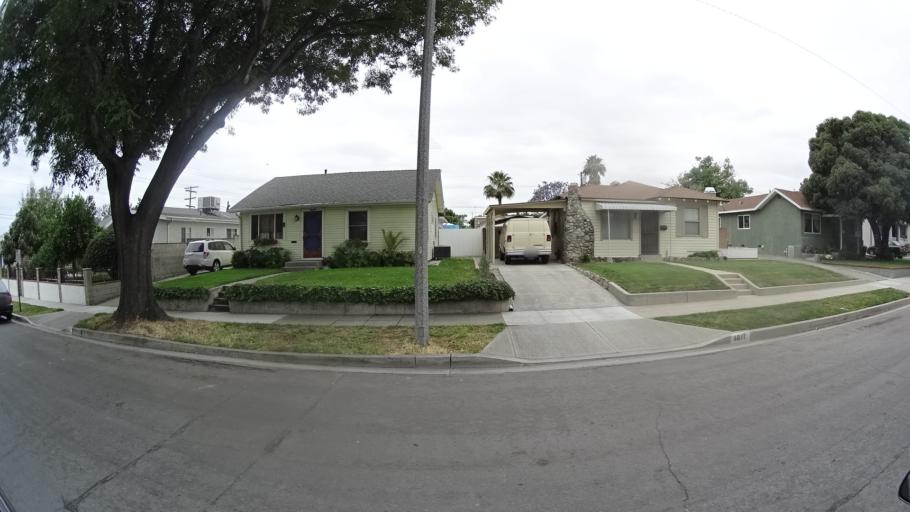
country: US
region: California
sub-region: Los Angeles County
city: Burbank
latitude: 34.1886
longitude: -118.3371
